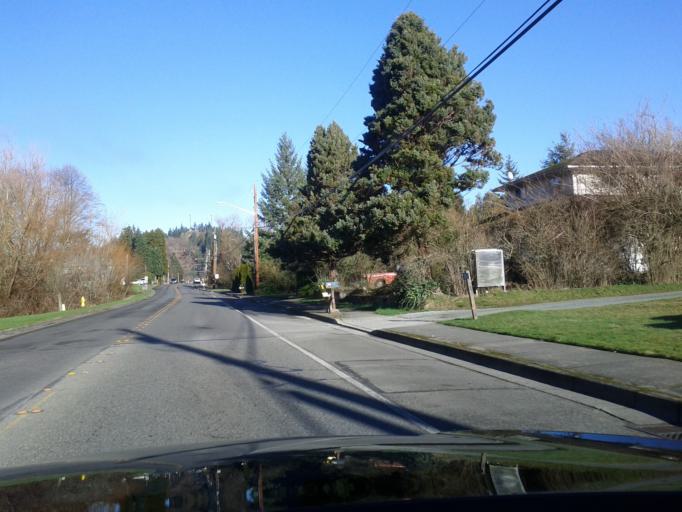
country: US
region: Washington
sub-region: Skagit County
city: Burlington
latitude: 48.4678
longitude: -122.3248
